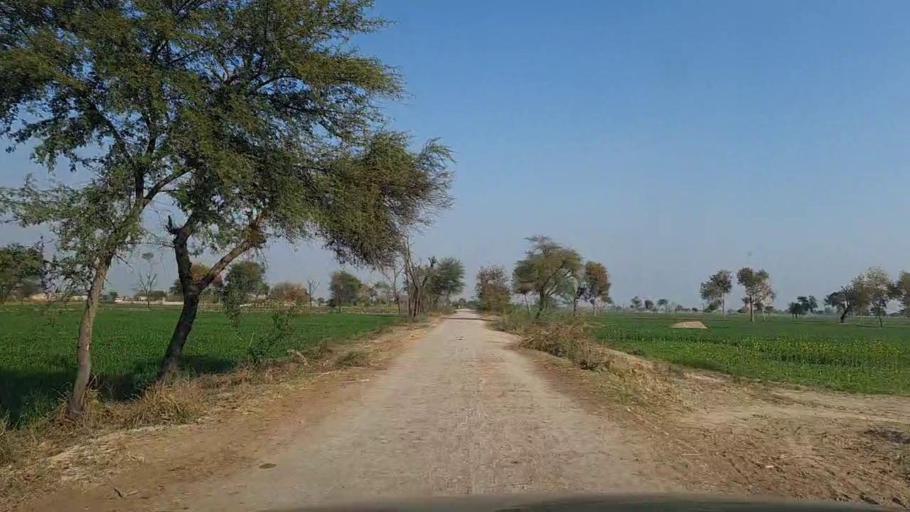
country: PK
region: Sindh
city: Nawabshah
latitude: 26.3873
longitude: 68.4581
